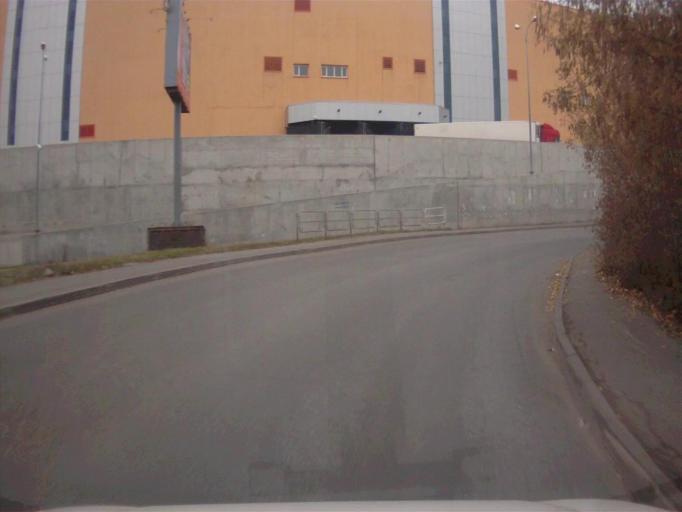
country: RU
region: Chelyabinsk
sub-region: Gorod Chelyabinsk
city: Chelyabinsk
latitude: 55.1709
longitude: 61.3536
